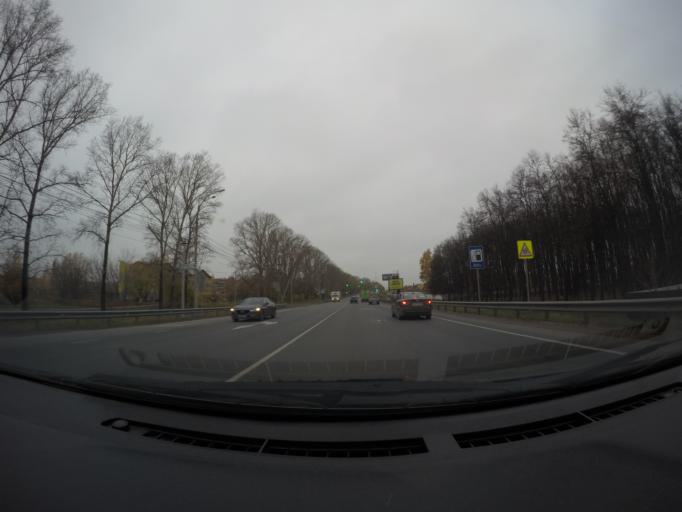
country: RU
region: Moskovskaya
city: Bronnitsy
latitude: 55.4145
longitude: 38.2718
